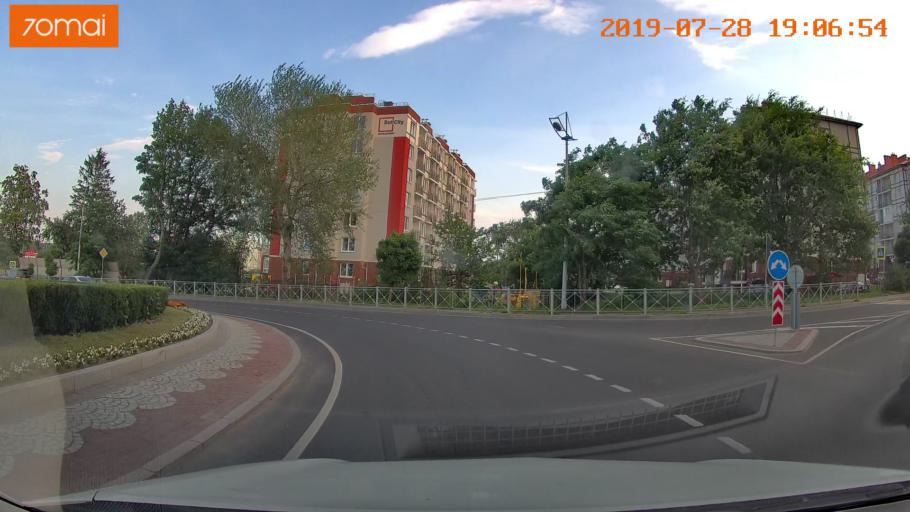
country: RU
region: Kaliningrad
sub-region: Gorod Svetlogorsk
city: Svetlogorsk
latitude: 54.9294
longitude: 20.1677
